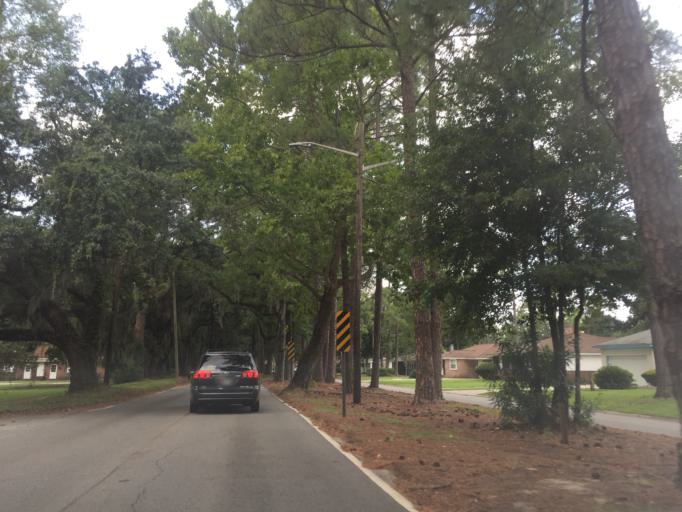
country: US
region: Georgia
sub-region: Chatham County
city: Savannah
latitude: 32.0332
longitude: -81.1094
